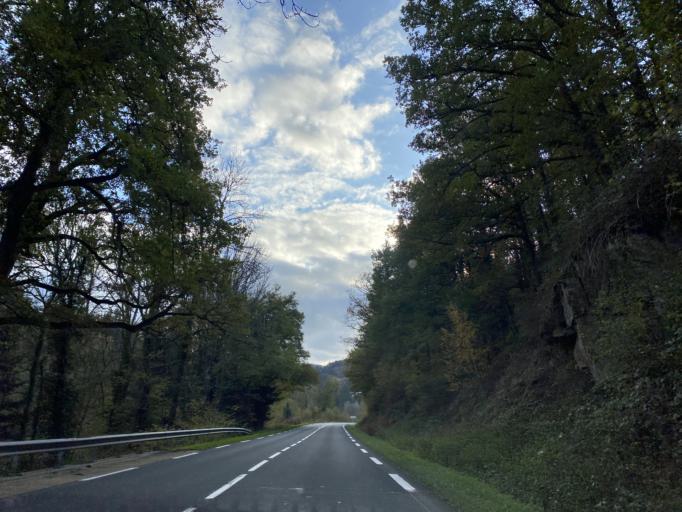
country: FR
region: Auvergne
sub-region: Departement du Puy-de-Dome
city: Job
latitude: 45.6483
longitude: 3.6735
